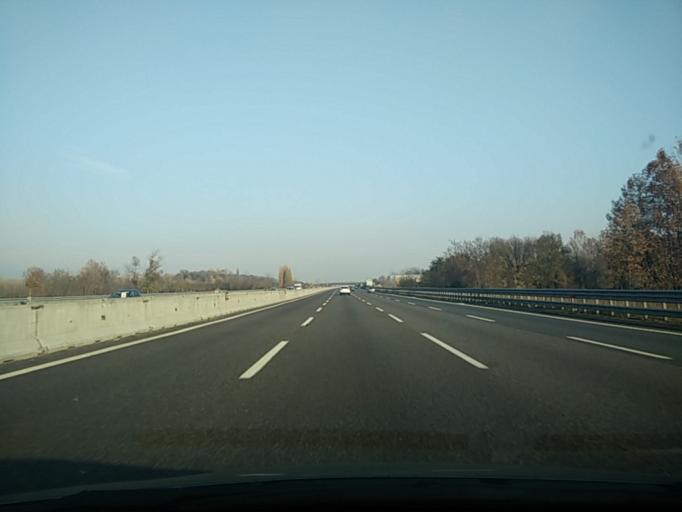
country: IT
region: Lombardy
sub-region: Provincia di Bergamo
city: Brembate
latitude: 45.6157
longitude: 9.5611
